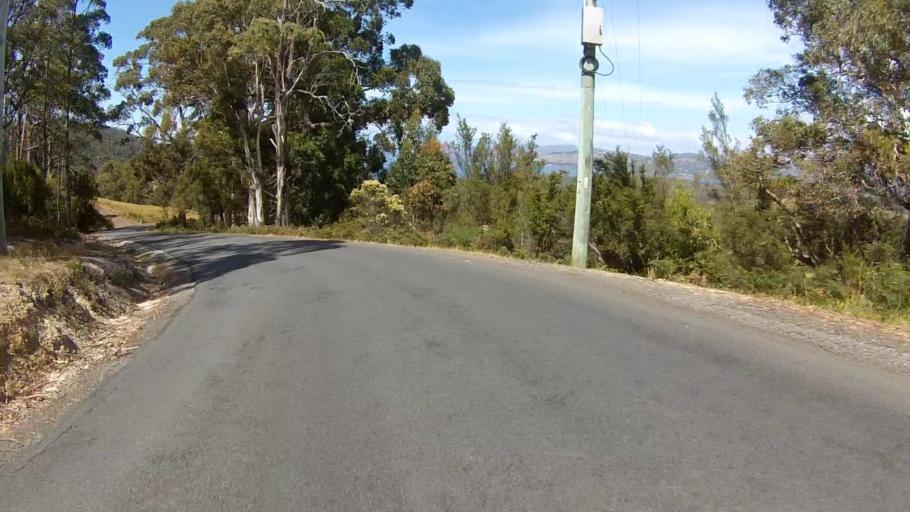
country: AU
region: Tasmania
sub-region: Huon Valley
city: Cygnet
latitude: -43.2295
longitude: 147.1301
